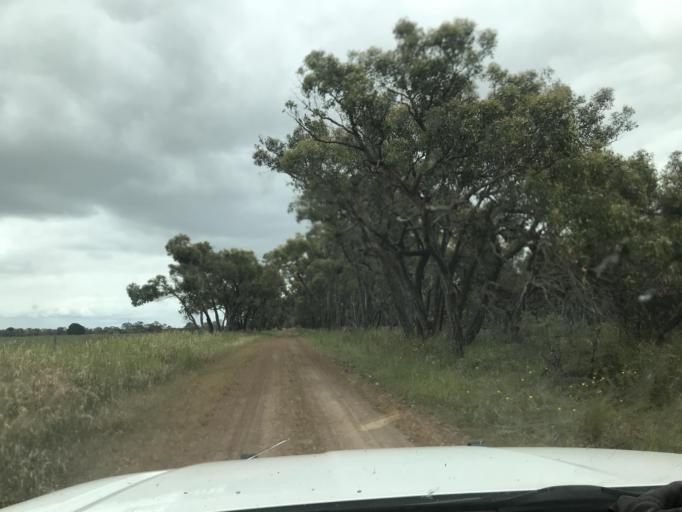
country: AU
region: South Australia
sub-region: Wattle Range
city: Penola
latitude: -37.0986
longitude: 141.2767
